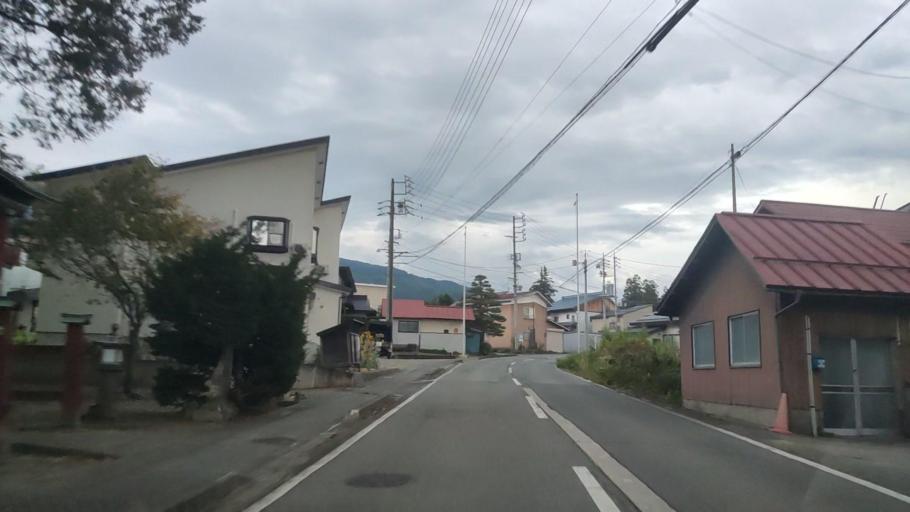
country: JP
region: Nagano
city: Iiyama
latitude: 36.8570
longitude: 138.4086
